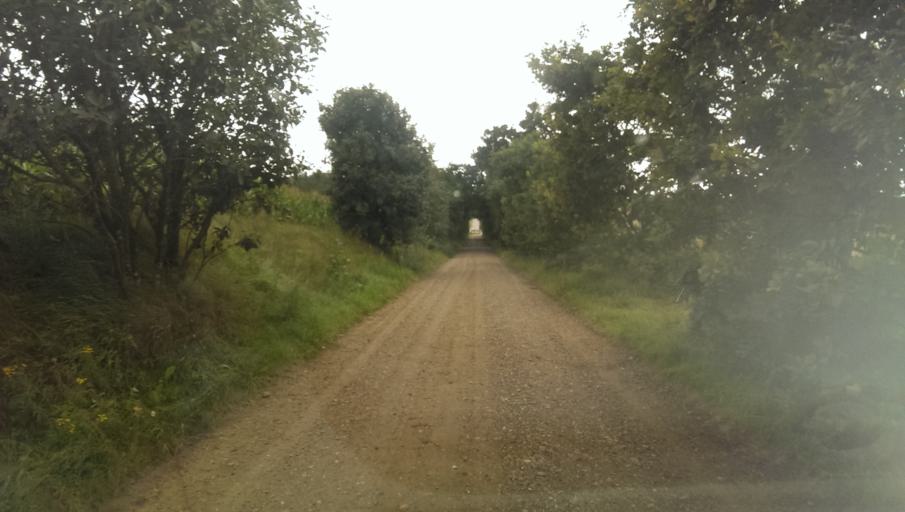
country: DK
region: South Denmark
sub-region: Esbjerg Kommune
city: Tjaereborg
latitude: 55.4712
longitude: 8.5942
